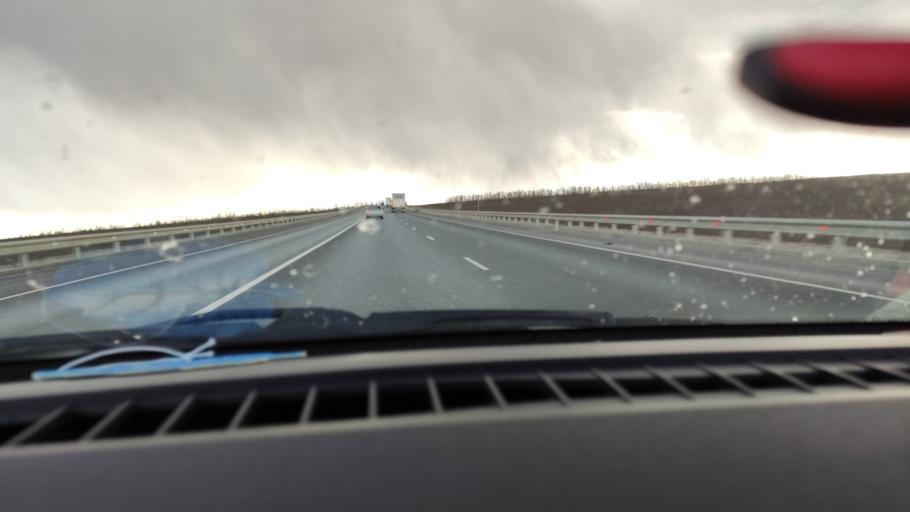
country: RU
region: Saratov
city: Yelshanka
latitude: 51.8375
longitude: 46.4739
